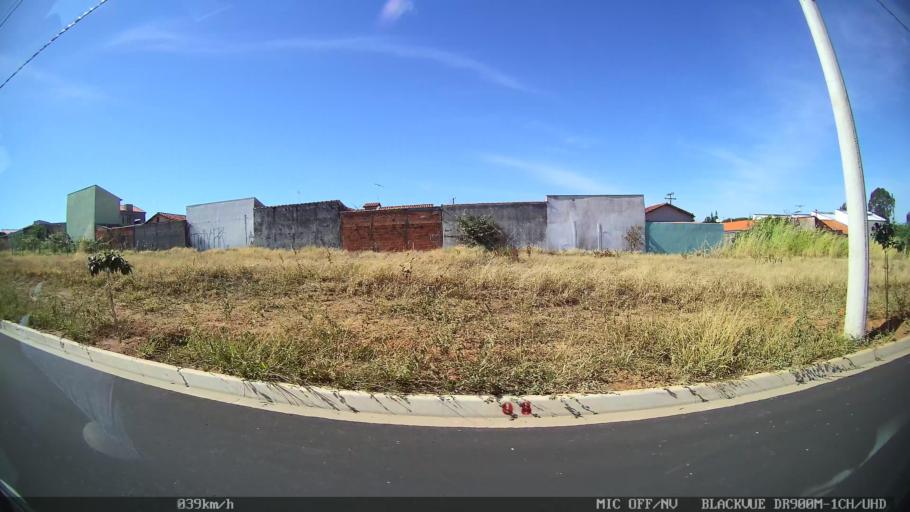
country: BR
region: Sao Paulo
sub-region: Franca
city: Franca
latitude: -20.5559
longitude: -47.3651
